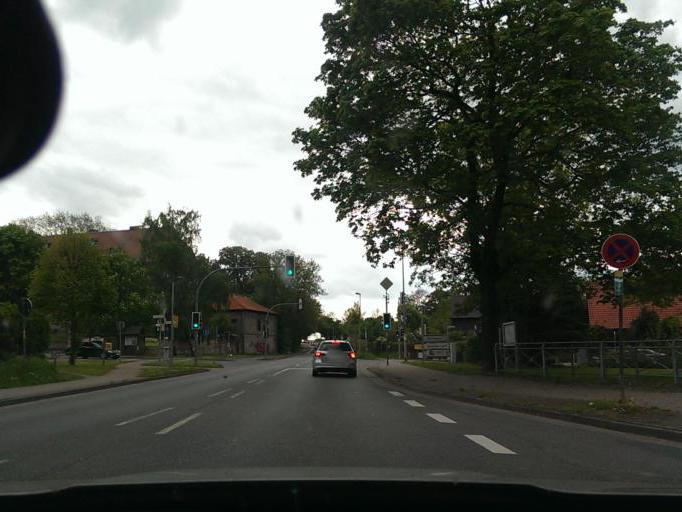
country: DE
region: Lower Saxony
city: Pattensen
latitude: 52.2746
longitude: 9.7952
